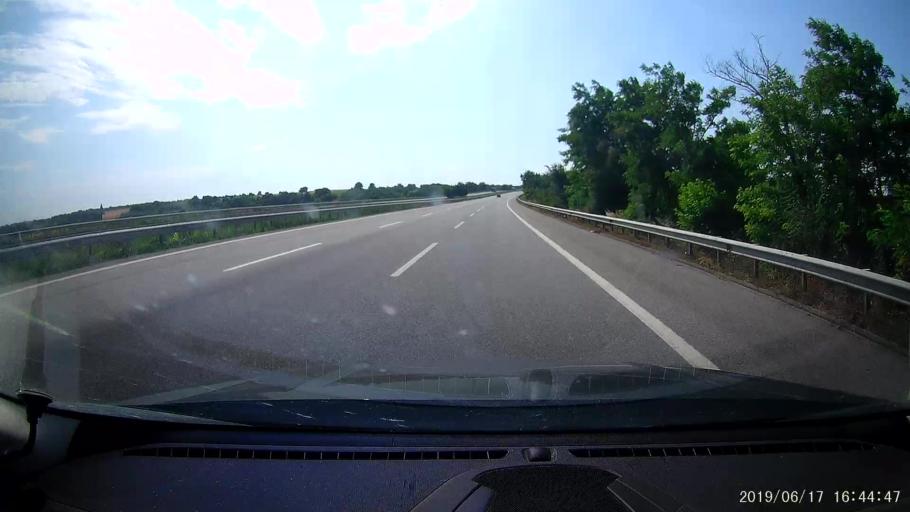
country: TR
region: Kirklareli
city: Luleburgaz
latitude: 41.4823
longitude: 27.2505
